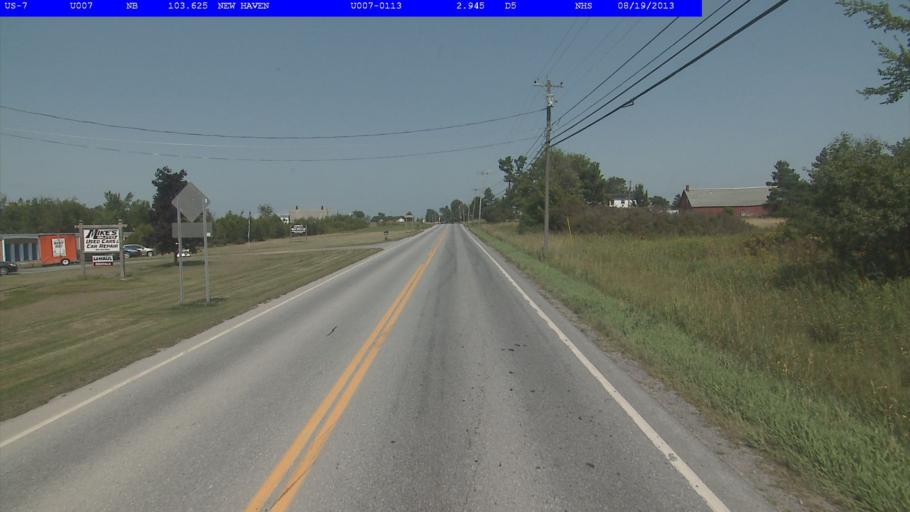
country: US
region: Vermont
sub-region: Addison County
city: Middlebury (village)
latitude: 44.0879
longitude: -73.1752
